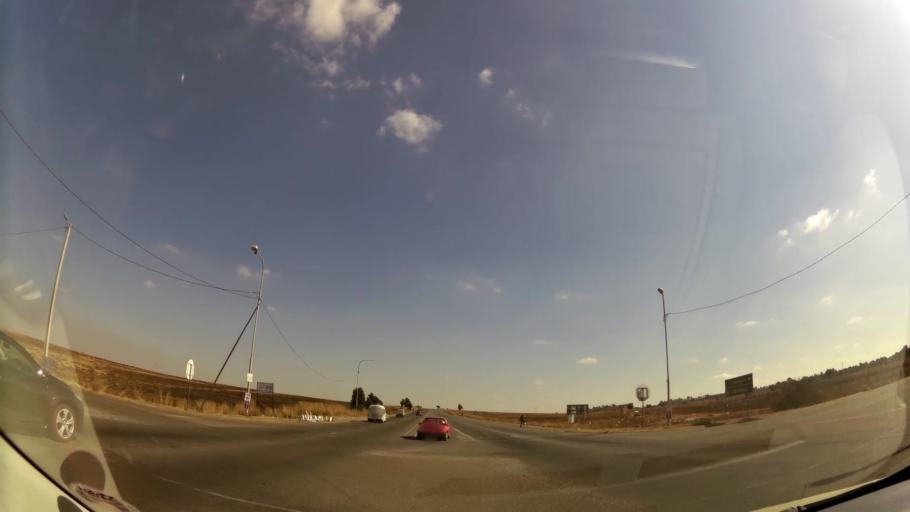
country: ZA
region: Gauteng
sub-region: West Rand District Municipality
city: Randfontein
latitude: -26.1815
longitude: 27.7497
